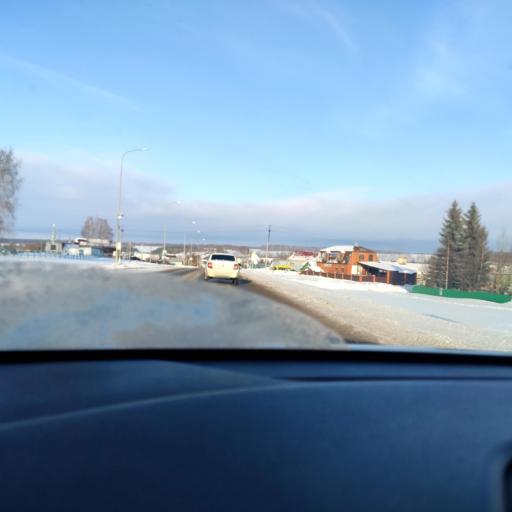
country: RU
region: Tatarstan
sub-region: Arskiy Rayon
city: Arsk
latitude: 56.1353
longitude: 49.9157
